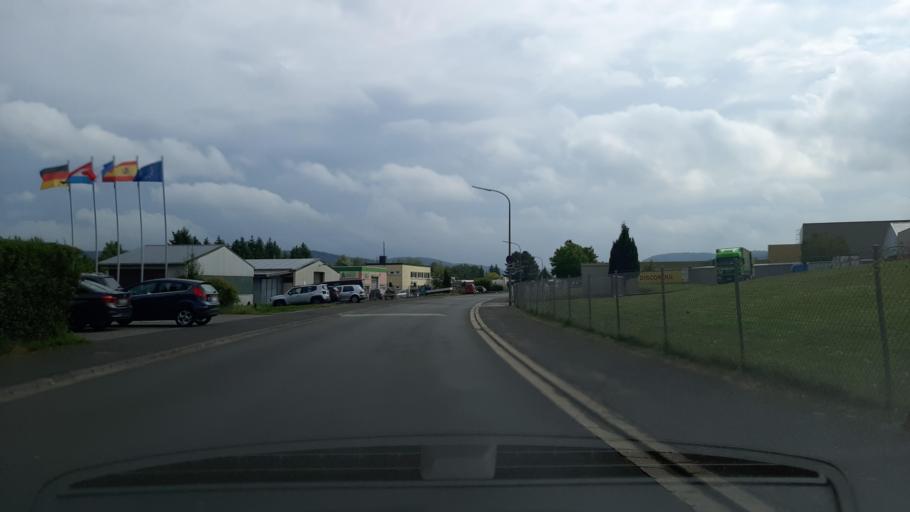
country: DE
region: Rheinland-Pfalz
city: Briedel
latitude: 50.0315
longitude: 7.1601
